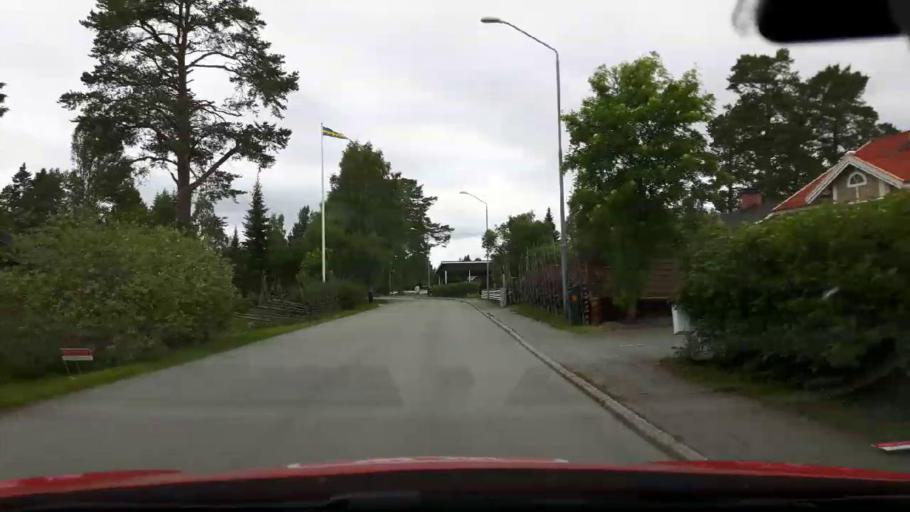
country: SE
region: Jaemtland
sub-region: OEstersunds Kommun
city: Ostersund
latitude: 63.2067
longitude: 14.6232
